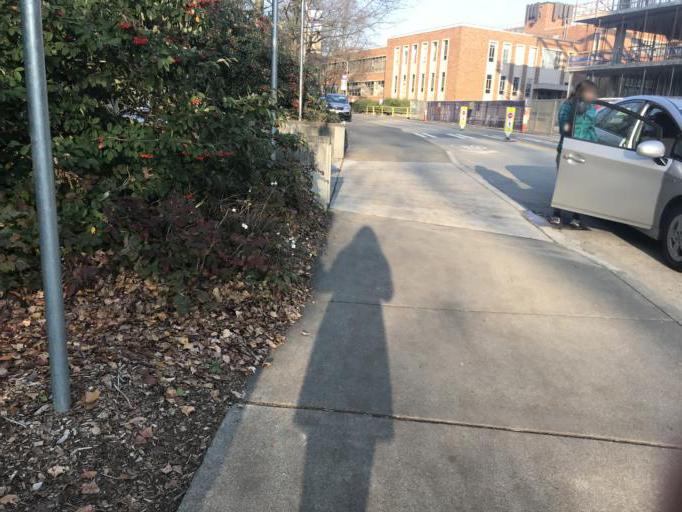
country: US
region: Washington
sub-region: King County
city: Seattle
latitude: 47.6527
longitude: -122.3044
